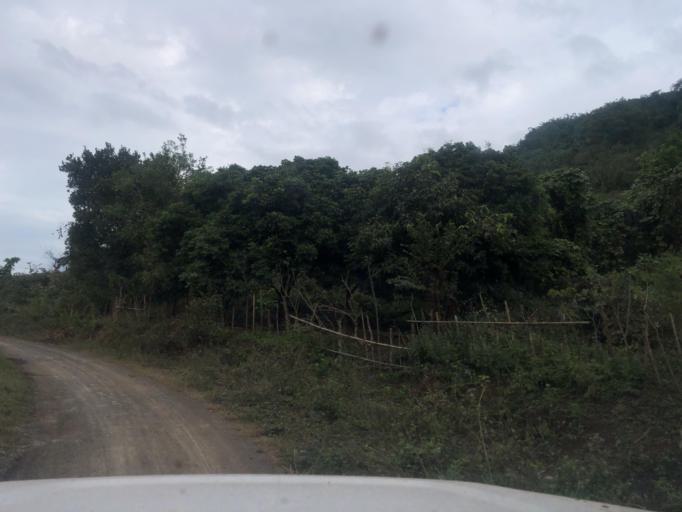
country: LA
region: Phongsali
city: Khoa
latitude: 21.2961
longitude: 102.5869
